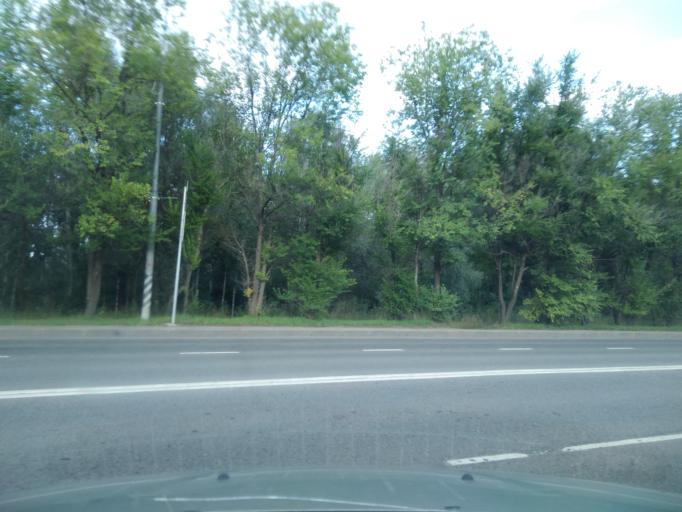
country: RU
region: Moscow
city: Strogino
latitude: 55.8176
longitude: 37.4035
